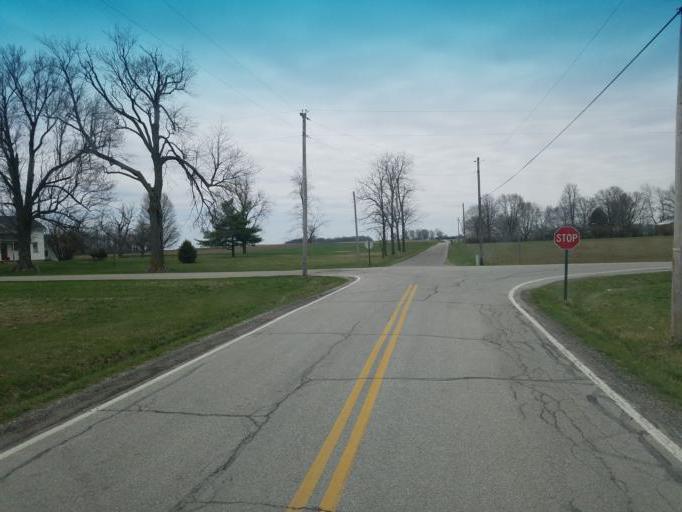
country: US
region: Ohio
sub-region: Crawford County
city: Bucyrus
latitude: 40.8656
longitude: -82.9405
